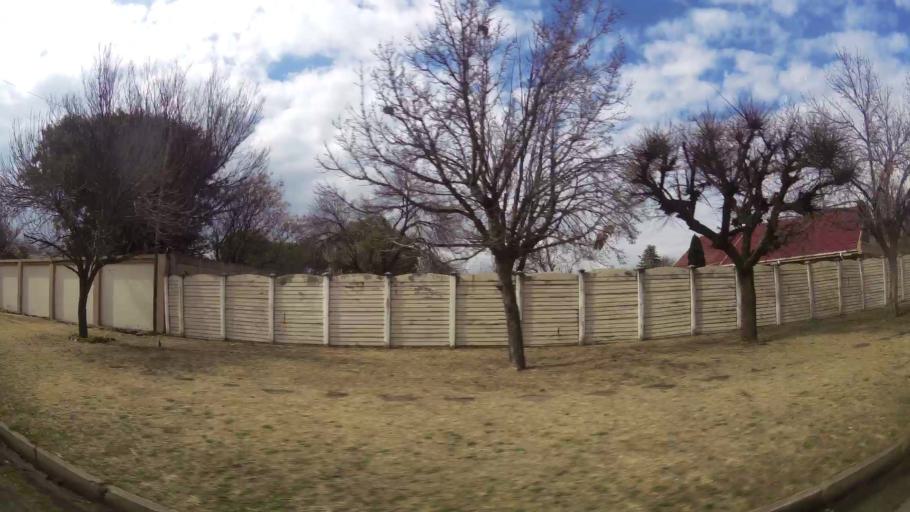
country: ZA
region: Gauteng
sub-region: Sedibeng District Municipality
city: Vereeniging
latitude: -26.6524
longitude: 27.9739
